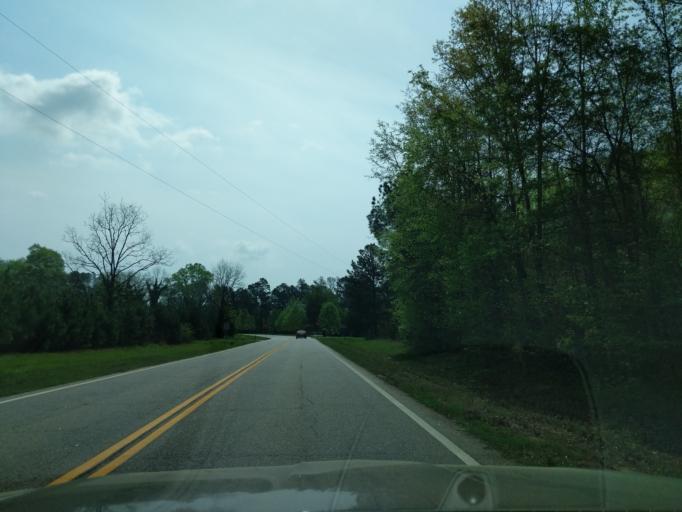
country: US
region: Georgia
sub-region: Lincoln County
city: Lincolnton
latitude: 33.7738
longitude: -82.3761
